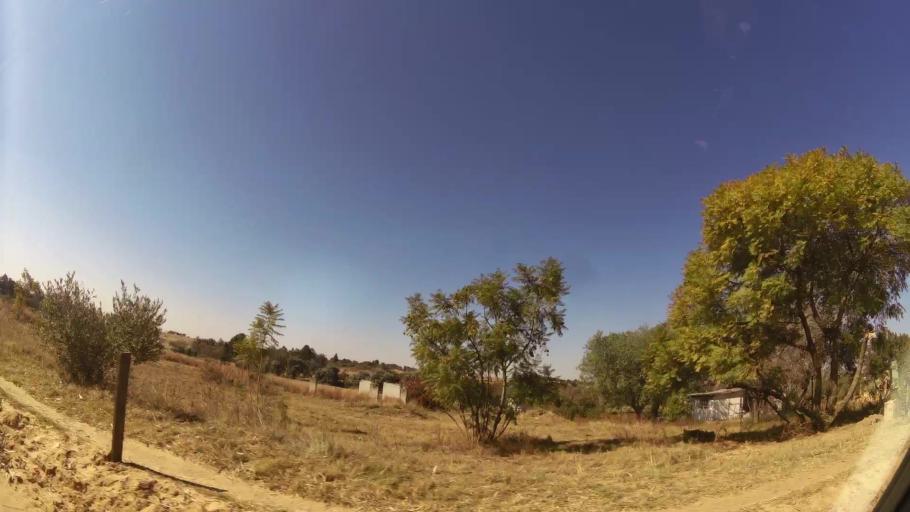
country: ZA
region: Gauteng
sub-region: City of Johannesburg Metropolitan Municipality
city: Midrand
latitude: -25.9373
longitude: 28.0869
